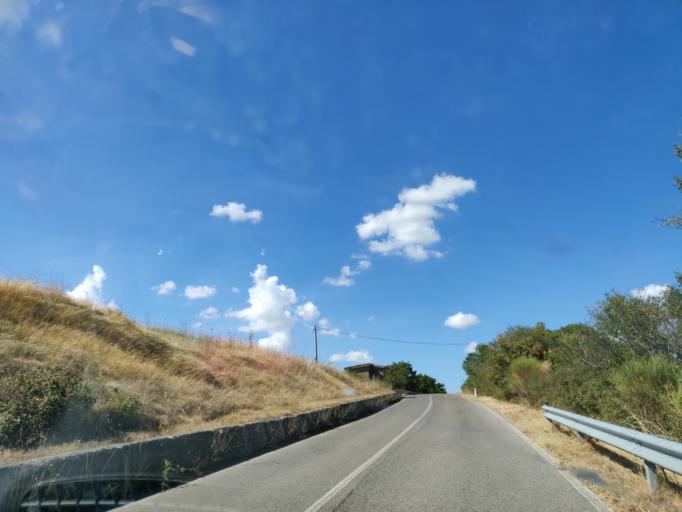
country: IT
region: Tuscany
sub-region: Provincia di Siena
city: Radicofani
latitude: 42.9334
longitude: 11.7321
